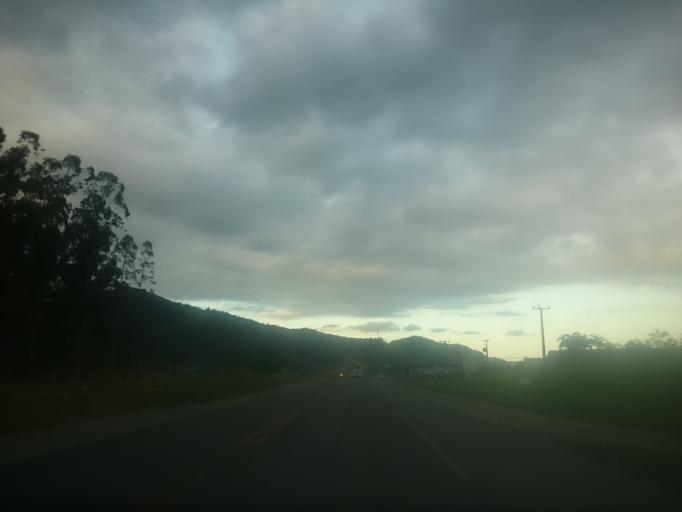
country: BR
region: Santa Catarina
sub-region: Gaspar
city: Gaspar
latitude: -26.8994
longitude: -48.9272
